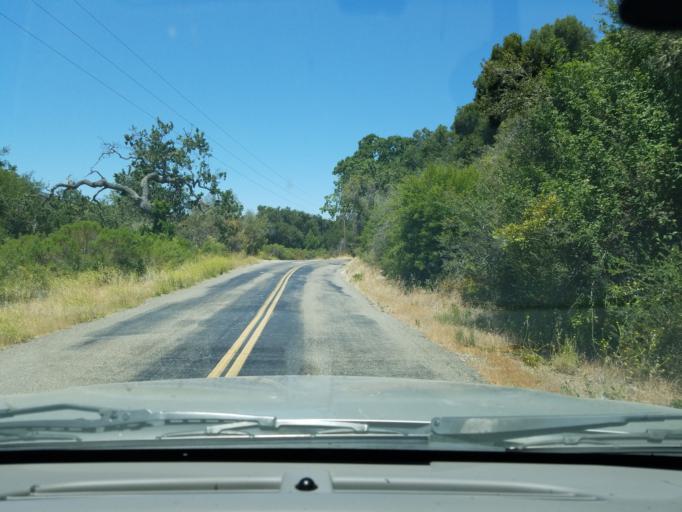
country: US
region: California
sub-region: Monterey County
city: Carmel Valley Village
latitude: 36.4221
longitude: -121.6149
